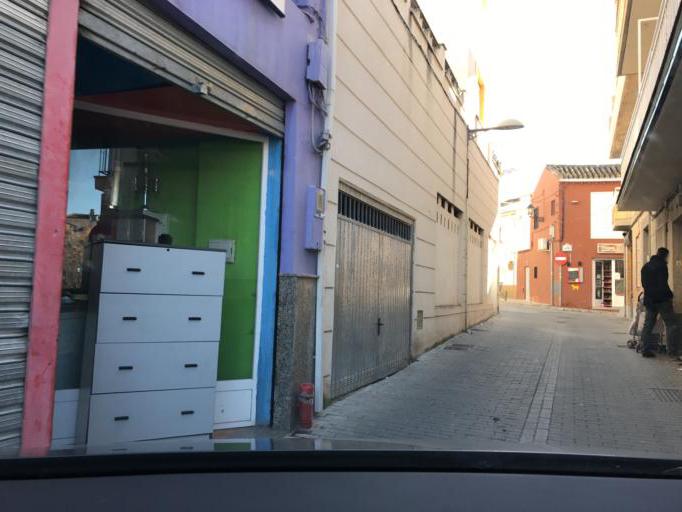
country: ES
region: Andalusia
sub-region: Provincia de Granada
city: Pulianas
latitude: 37.2229
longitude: -3.6065
